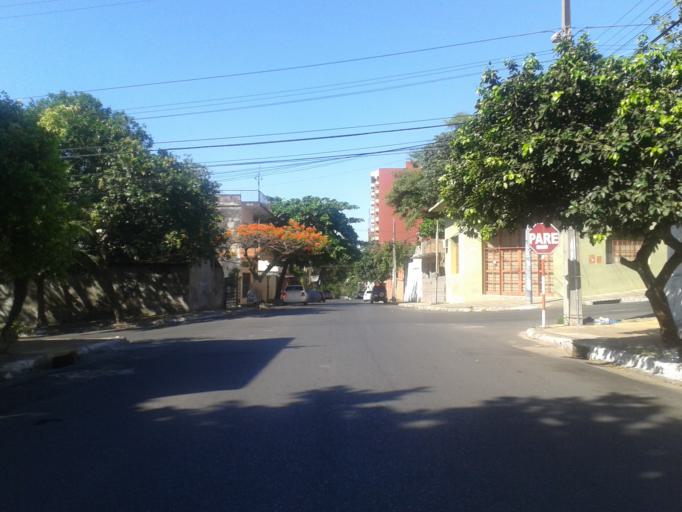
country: PY
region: Asuncion
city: Asuncion
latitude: -25.2902
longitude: -57.6431
